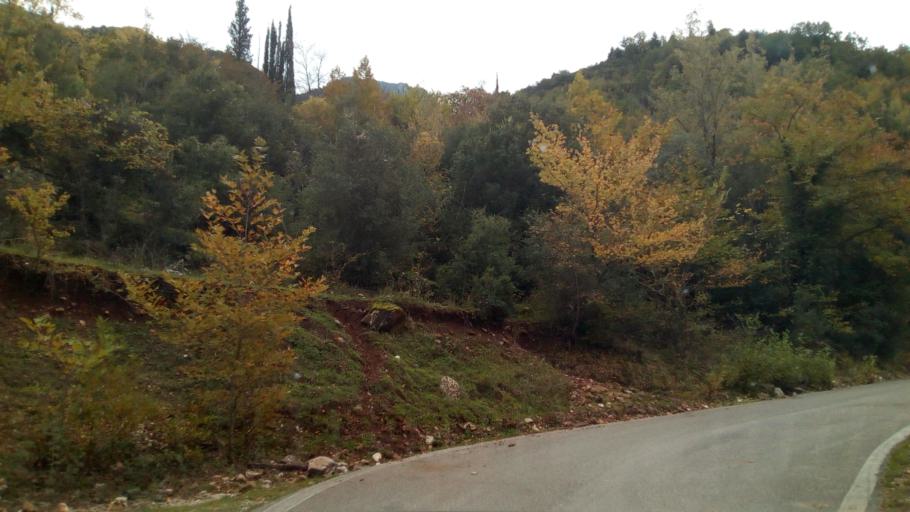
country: GR
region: West Greece
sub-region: Nomos Aitolias kai Akarnanias
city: Thermo
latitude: 38.5973
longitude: 21.8529
